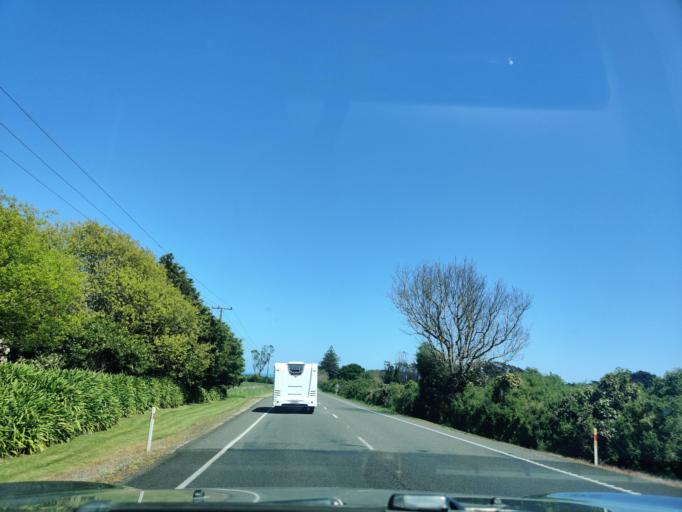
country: NZ
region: Taranaki
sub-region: South Taranaki District
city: Patea
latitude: -39.8075
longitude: 174.7576
